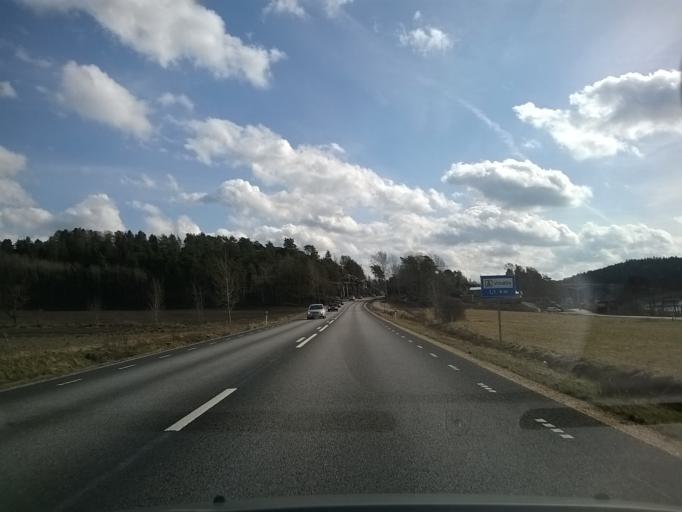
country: SE
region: Vaestra Goetaland
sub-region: Orust
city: Henan
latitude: 58.3117
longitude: 11.6935
